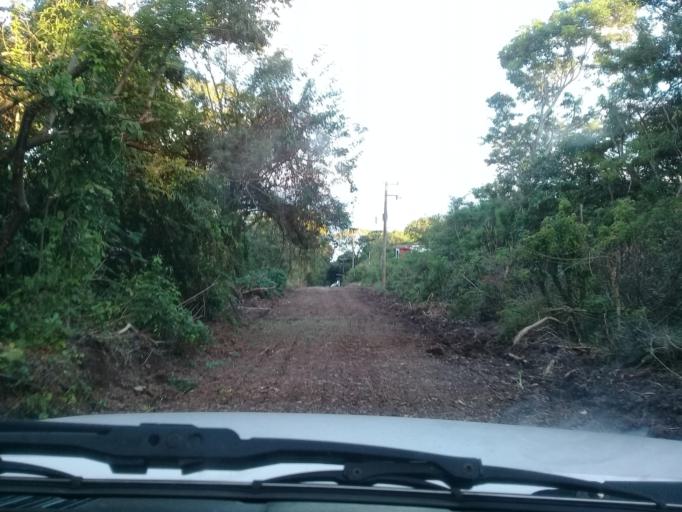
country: MX
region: Veracruz
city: Catemaco
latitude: 18.4366
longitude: -95.0835
